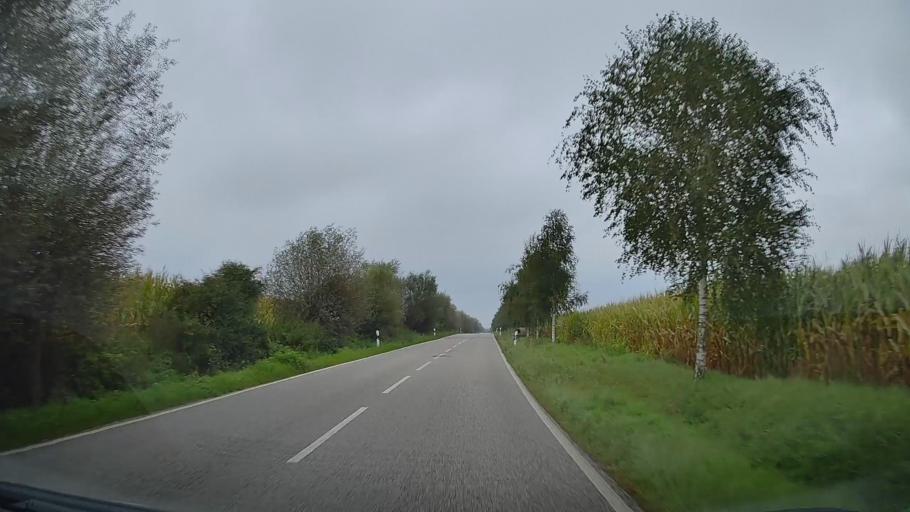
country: DE
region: Mecklenburg-Vorpommern
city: Blowatz
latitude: 53.9569
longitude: 11.5629
